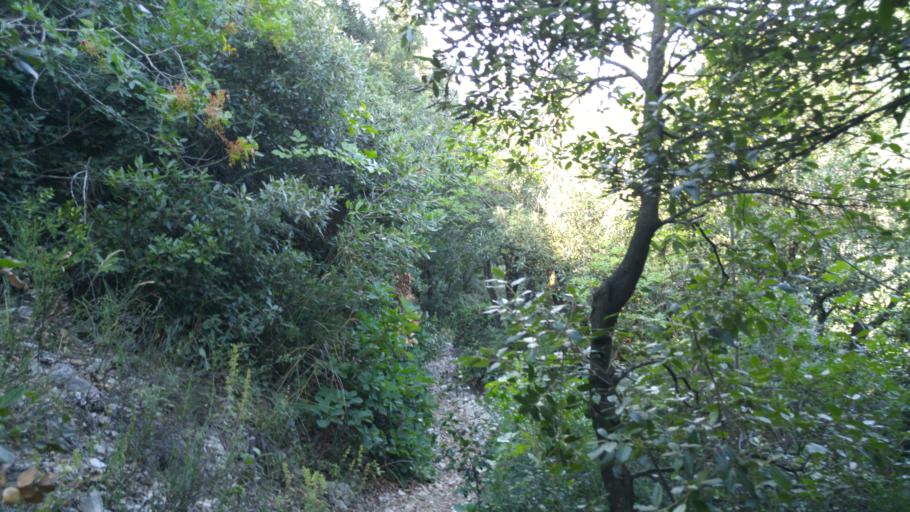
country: IT
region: The Marches
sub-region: Provincia di Pesaro e Urbino
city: Canavaccio
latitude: 43.6553
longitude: 12.7313
